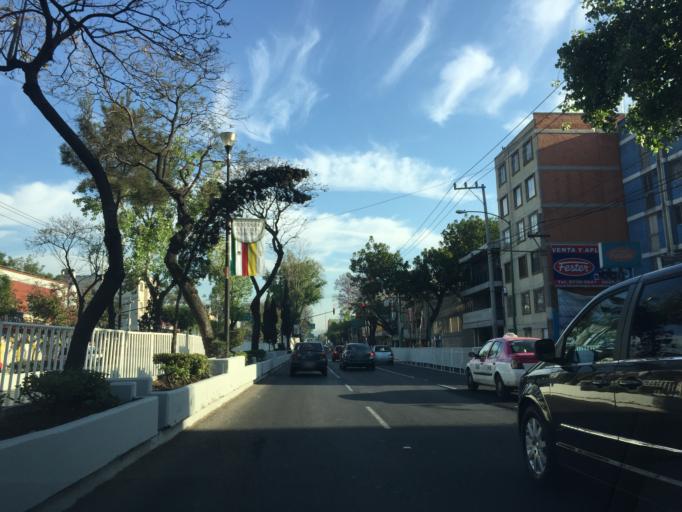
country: MX
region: Mexico City
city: Cuauhtemoc
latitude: 19.4583
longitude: -99.1275
